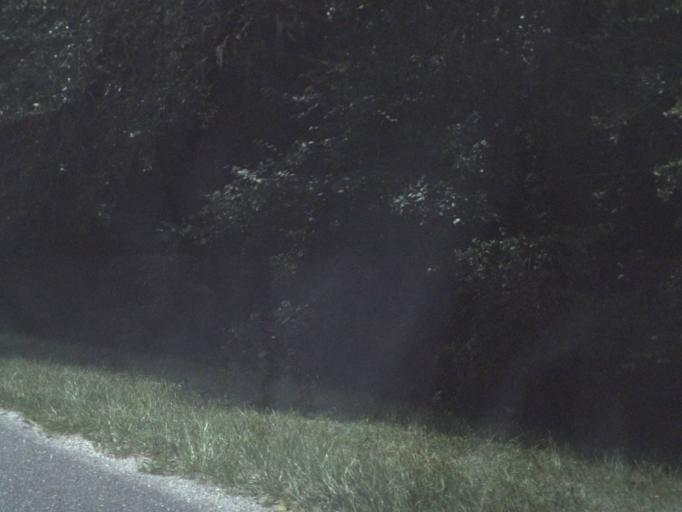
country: US
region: Florida
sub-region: Alachua County
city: High Springs
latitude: 29.8567
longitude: -82.6086
